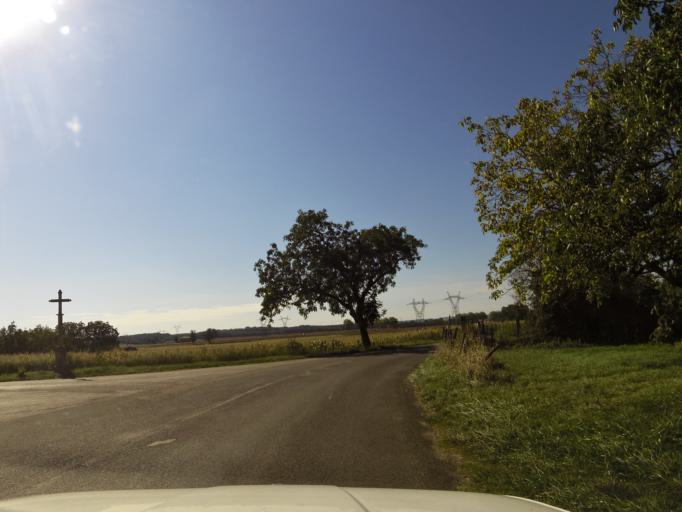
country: FR
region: Rhone-Alpes
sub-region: Departement de l'Ain
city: Vaux-en-Bugey
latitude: 45.9296
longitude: 5.3460
